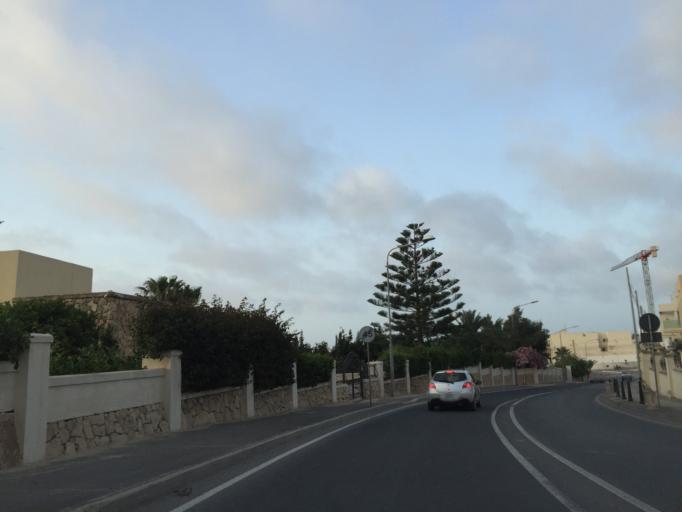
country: MT
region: Il-Mosta
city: Mosta
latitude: 35.9156
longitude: 14.4160
